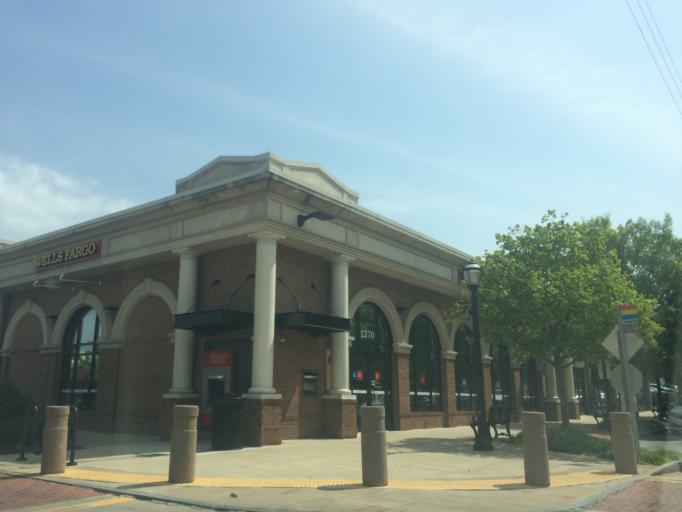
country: US
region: Georgia
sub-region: DeKalb County
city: Druid Hills
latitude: 33.7584
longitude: -84.3477
